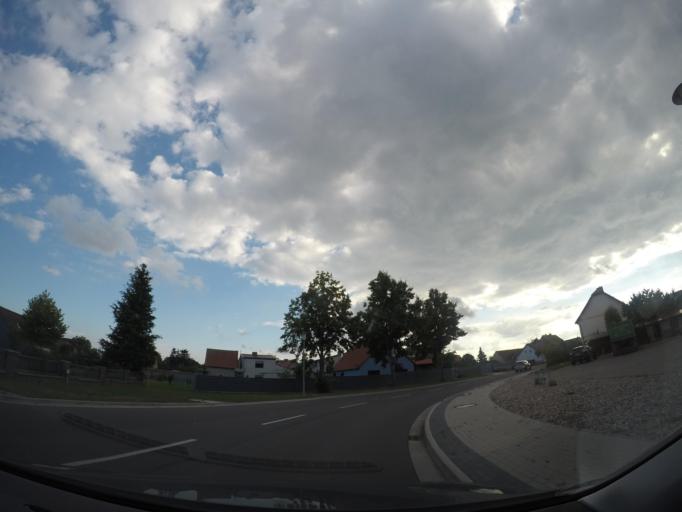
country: DE
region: Saxony-Anhalt
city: Mieste
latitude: 52.5057
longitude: 11.1416
